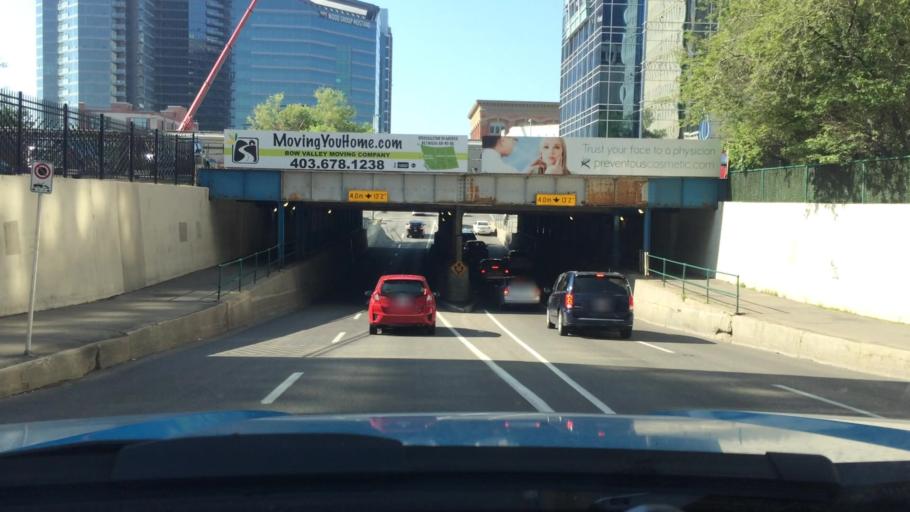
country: CA
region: Alberta
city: Calgary
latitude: 51.0443
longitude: -114.0607
